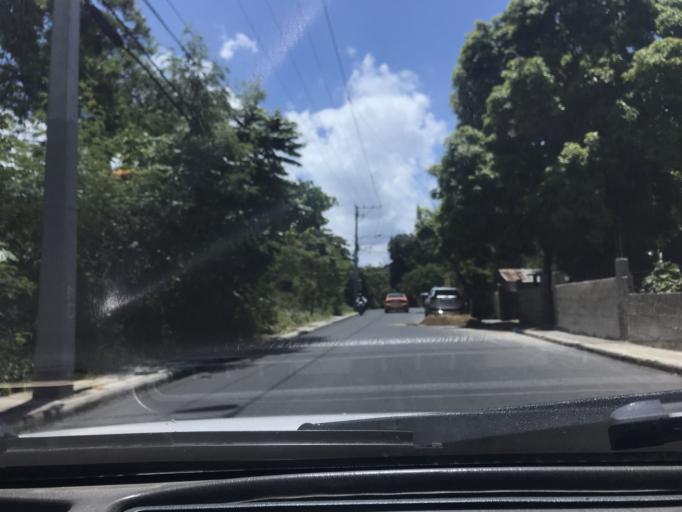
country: DO
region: Santiago
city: Santiago de los Caballeros
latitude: 19.4280
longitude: -70.7002
